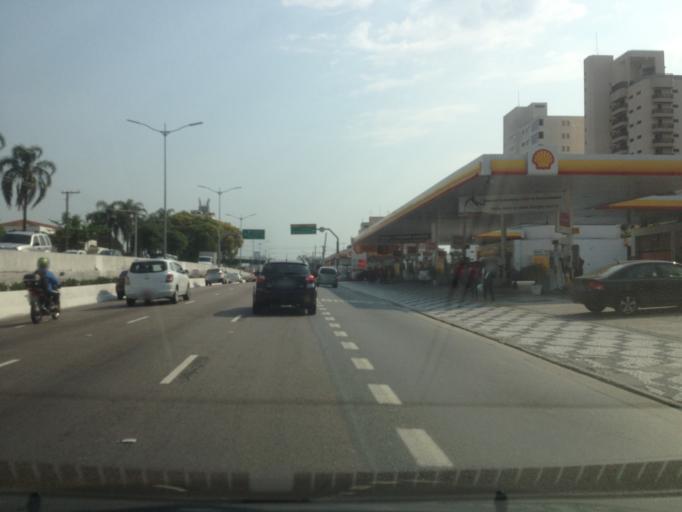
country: BR
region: Sao Paulo
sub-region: Sao Paulo
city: Sao Paulo
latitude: -23.6118
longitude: -46.6567
